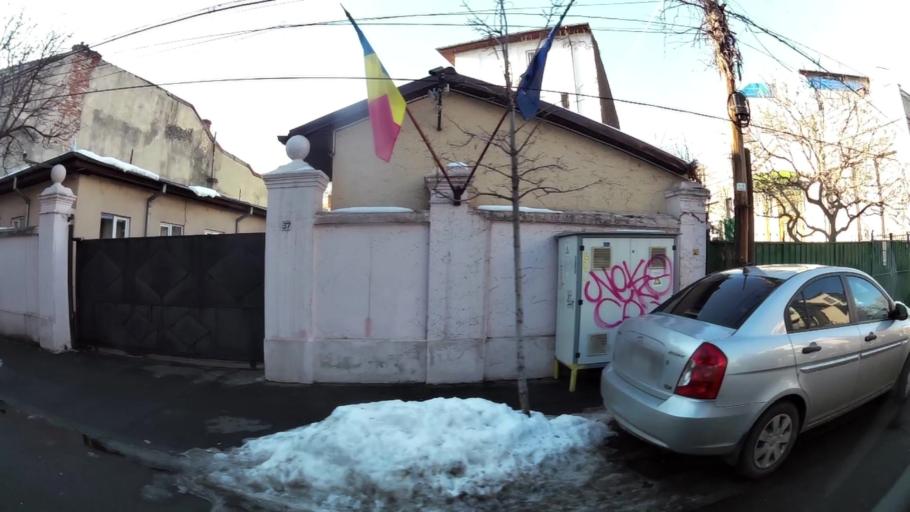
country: RO
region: Bucuresti
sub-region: Municipiul Bucuresti
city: Bucharest
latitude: 44.4431
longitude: 26.1131
